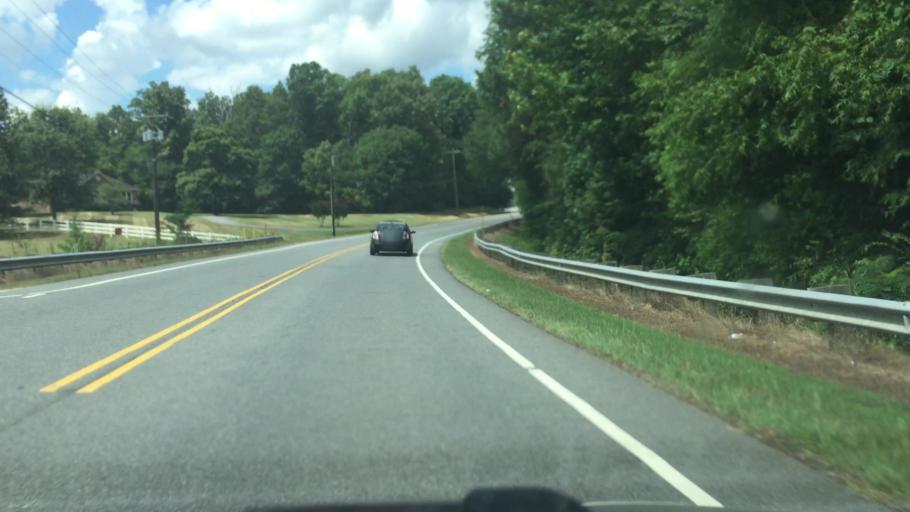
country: US
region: North Carolina
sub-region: Rowan County
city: Enochville
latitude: 35.4809
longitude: -80.7174
